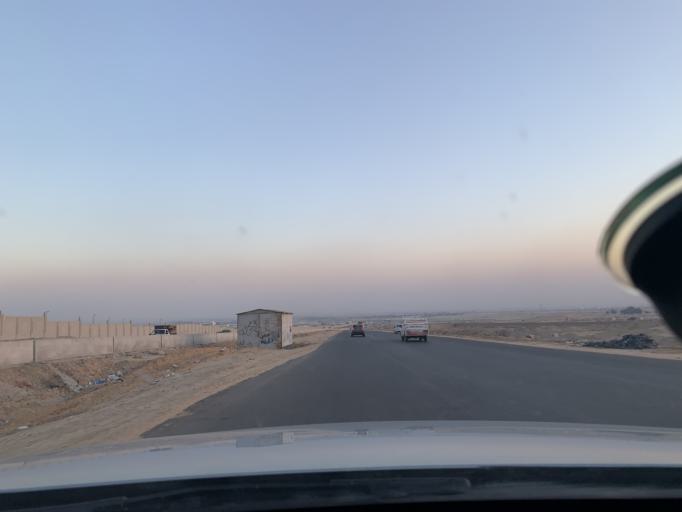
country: EG
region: Muhafazat al Qalyubiyah
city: Al Khankah
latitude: 30.2268
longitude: 31.4274
